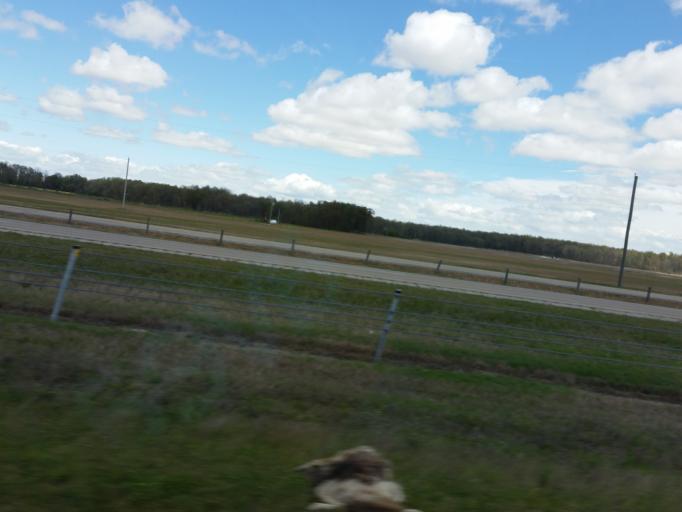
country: US
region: Arkansas
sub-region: Craighead County
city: Bay
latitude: 35.7919
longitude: -90.6111
